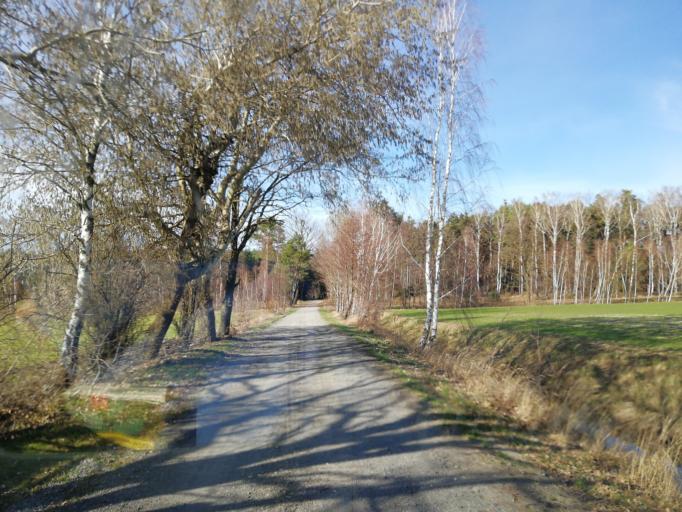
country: DE
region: Brandenburg
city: Ruckersdorf
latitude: 51.5611
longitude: 13.5912
